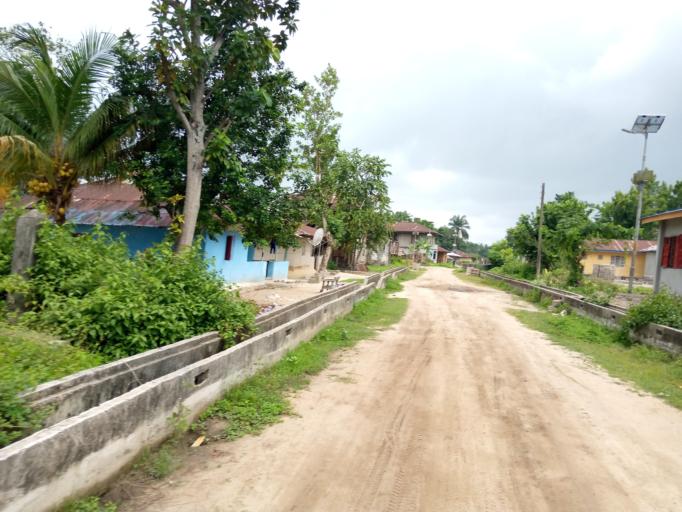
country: SL
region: Southern Province
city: Bonthe
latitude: 7.5312
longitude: -12.5030
